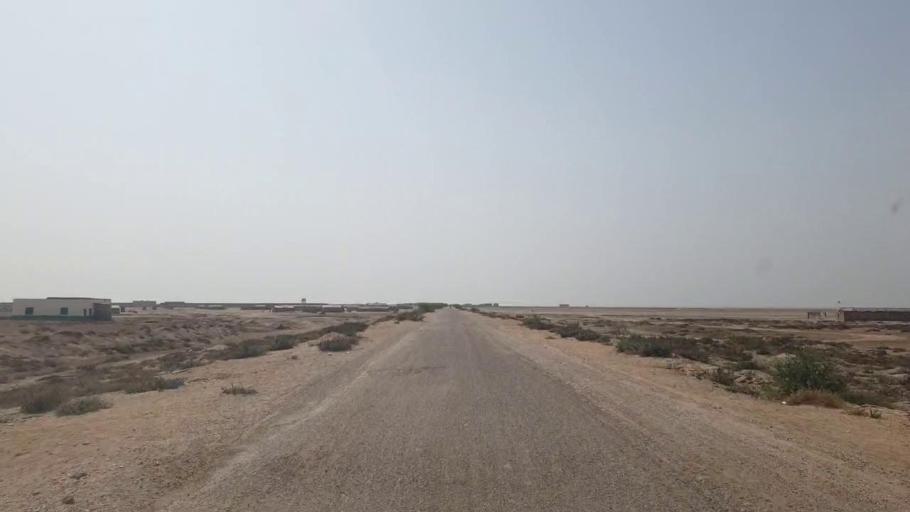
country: PK
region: Sindh
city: Jati
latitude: 24.3444
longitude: 68.5934
